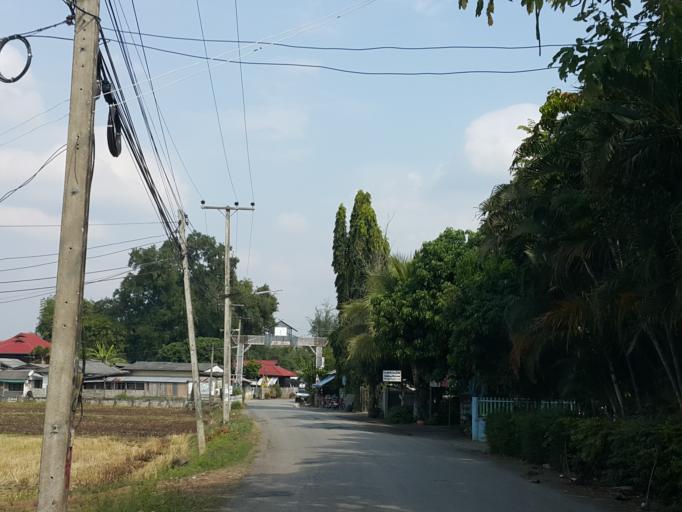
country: TH
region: Chiang Mai
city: San Kamphaeng
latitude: 18.8203
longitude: 99.1680
